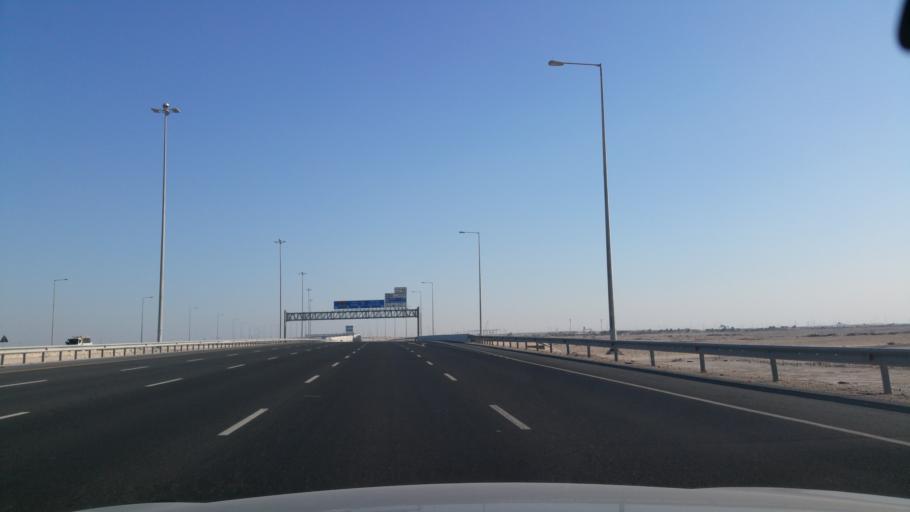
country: QA
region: Al Wakrah
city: Al Wukayr
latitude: 25.1371
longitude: 51.4771
